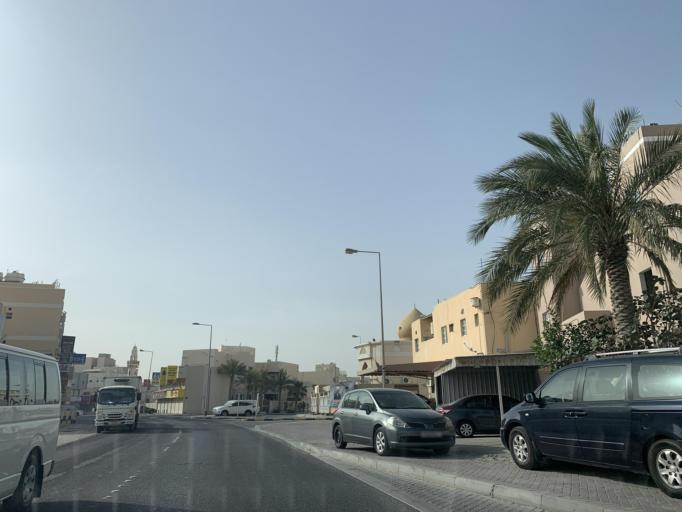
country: BH
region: Northern
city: Madinat `Isa
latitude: 26.1805
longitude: 50.5606
